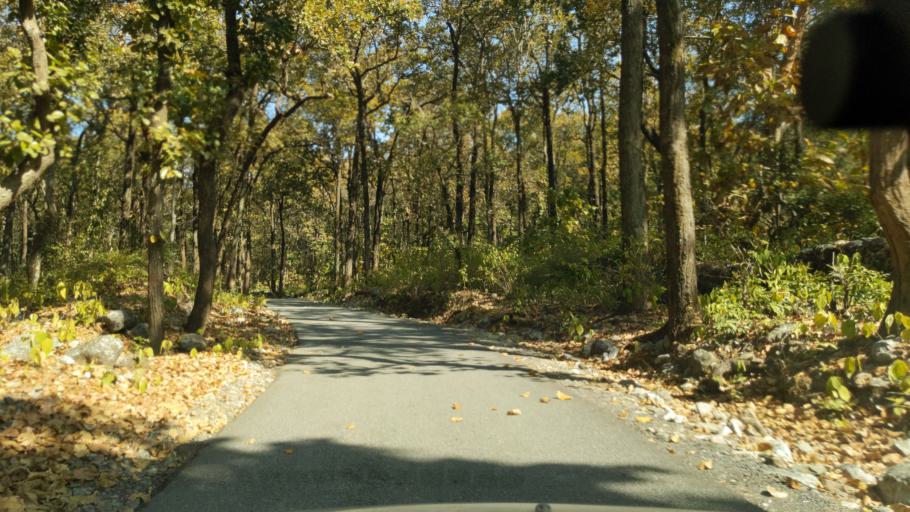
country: IN
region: Uttarakhand
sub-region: Naini Tal
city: Ramnagar
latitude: 29.4659
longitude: 79.2327
